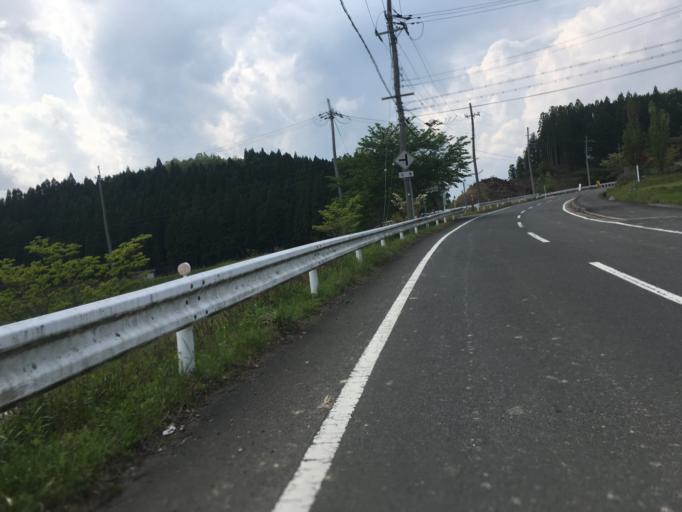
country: JP
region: Kyoto
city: Kameoka
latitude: 35.1109
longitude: 135.5743
